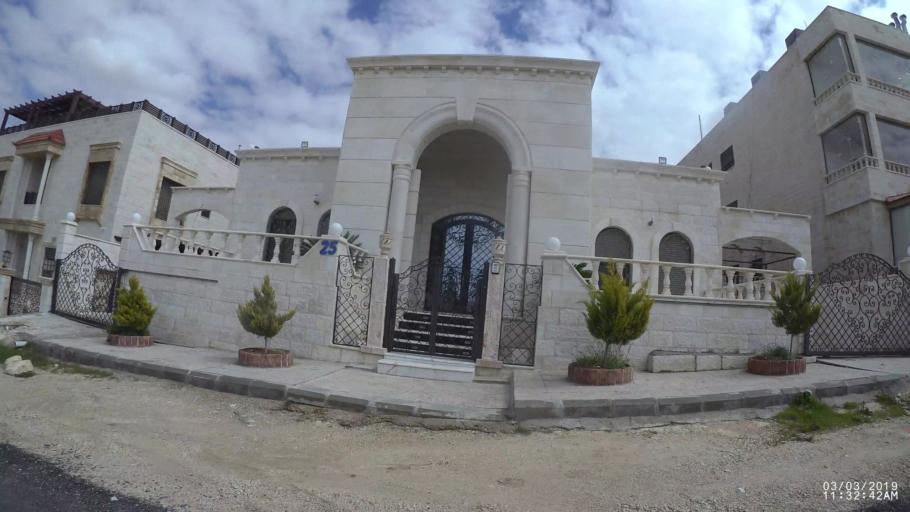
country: JO
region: Amman
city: Al Jubayhah
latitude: 32.0031
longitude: 35.9130
